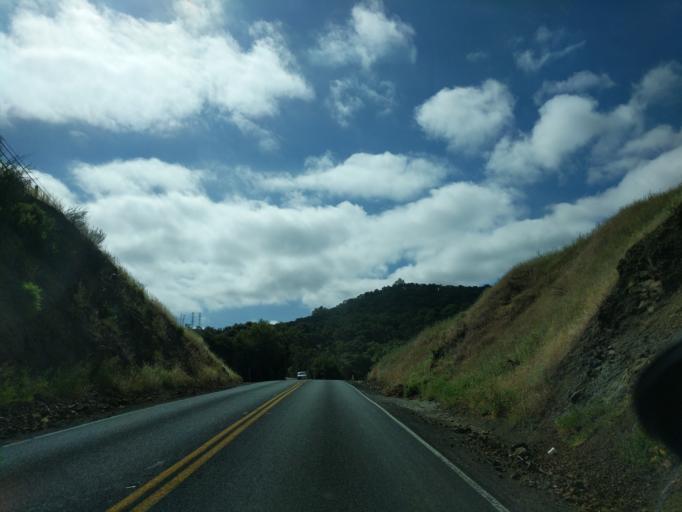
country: US
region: California
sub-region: Contra Costa County
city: Clayton
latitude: 37.9166
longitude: -121.8935
